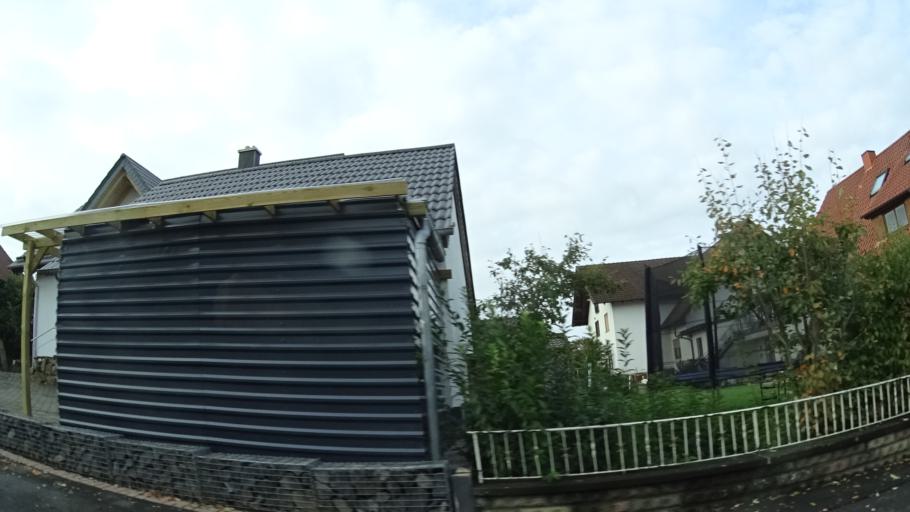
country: DE
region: Hesse
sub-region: Regierungsbezirk Kassel
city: Hofbieber
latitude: 50.5781
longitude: 9.8845
